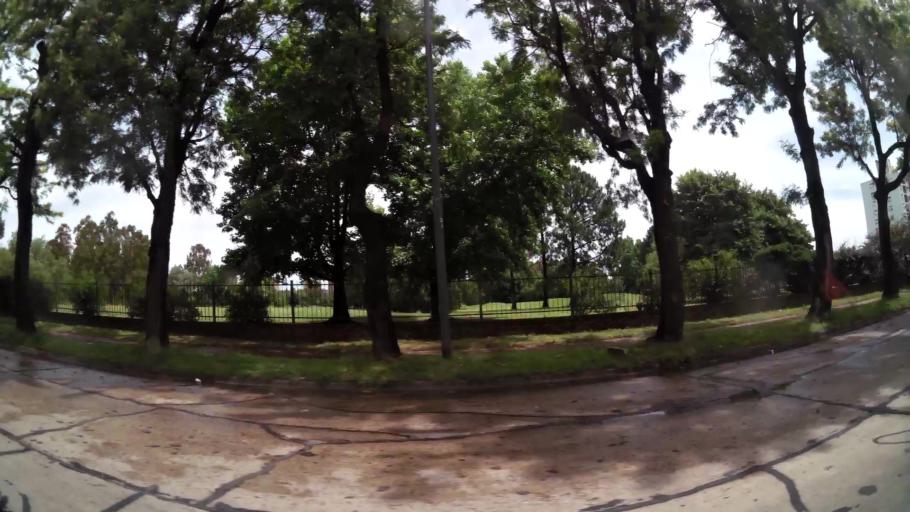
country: AR
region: Buenos Aires F.D.
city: Villa Lugano
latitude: -34.6767
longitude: -58.4548
